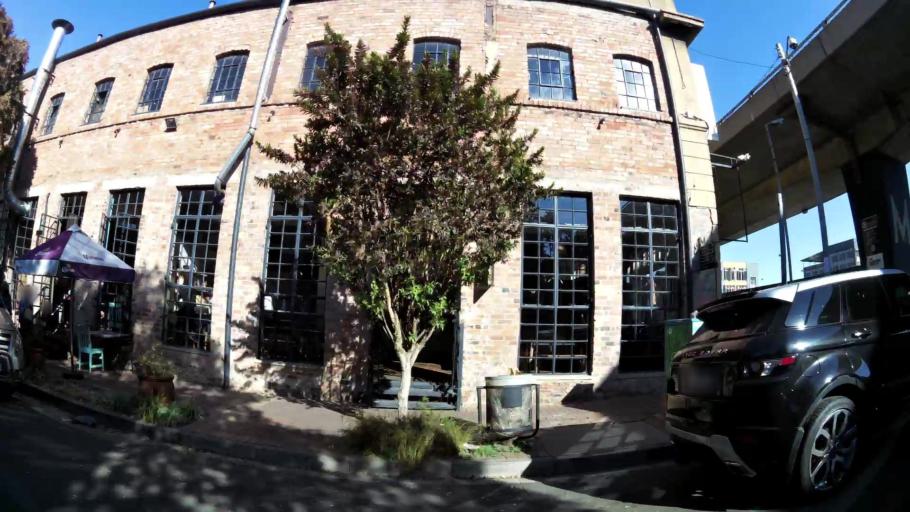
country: ZA
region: Gauteng
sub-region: City of Johannesburg Metropolitan Municipality
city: Johannesburg
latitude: -26.2043
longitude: 28.0575
